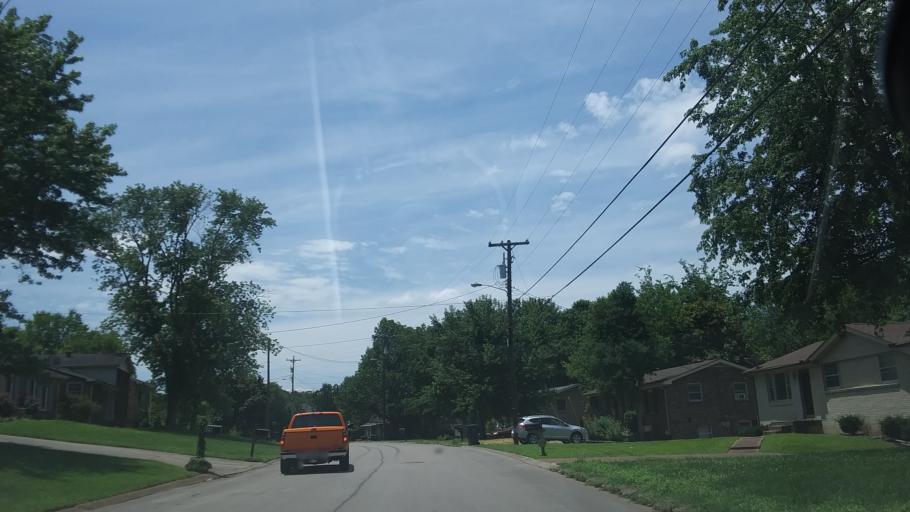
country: US
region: Tennessee
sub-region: Rutherford County
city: La Vergne
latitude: 36.0783
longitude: -86.6281
